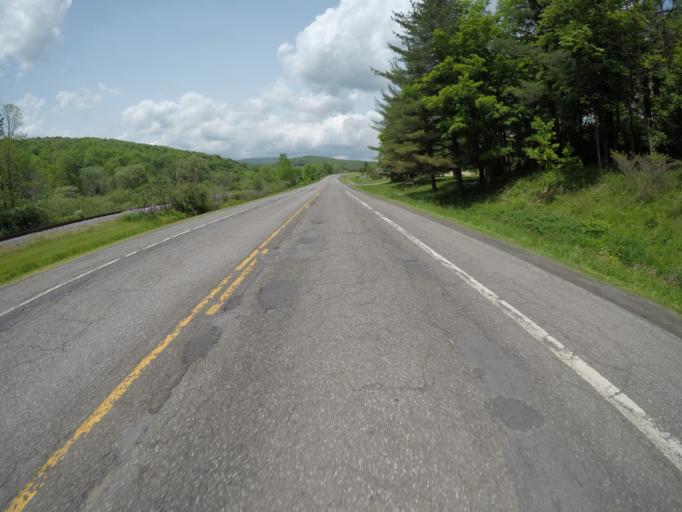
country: US
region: New York
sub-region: Delaware County
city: Stamford
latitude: 42.1997
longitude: -74.5984
